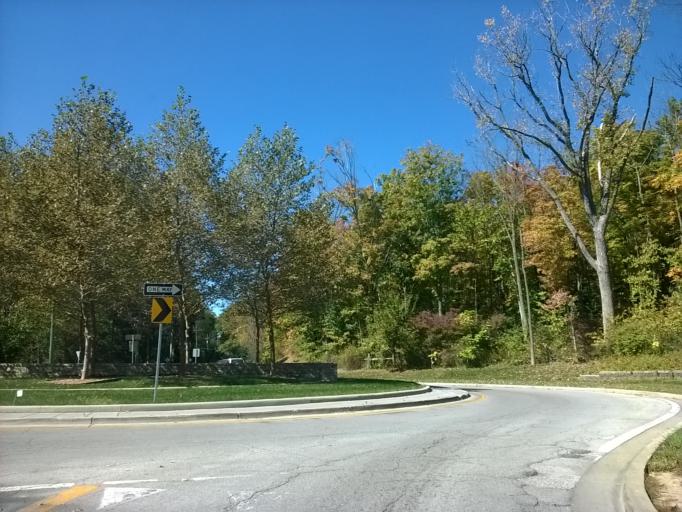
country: US
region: Indiana
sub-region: Hamilton County
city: Carmel
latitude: 39.9560
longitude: -86.1837
